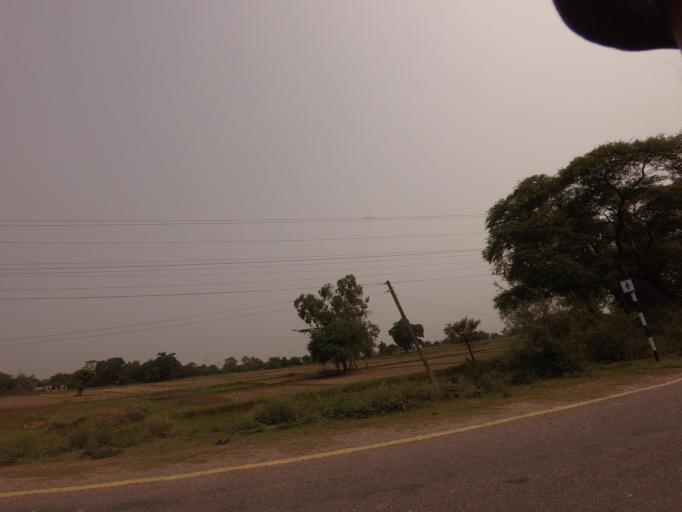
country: IN
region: Uttar Pradesh
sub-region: Maharajganj
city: Nautanwa
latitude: 27.5034
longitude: 83.3443
